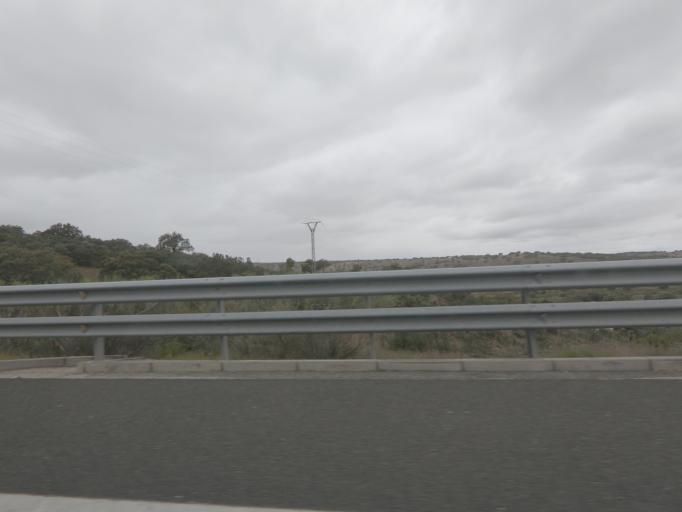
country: ES
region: Extremadura
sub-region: Provincia de Caceres
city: Mirabel
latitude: 39.8889
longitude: -6.2650
